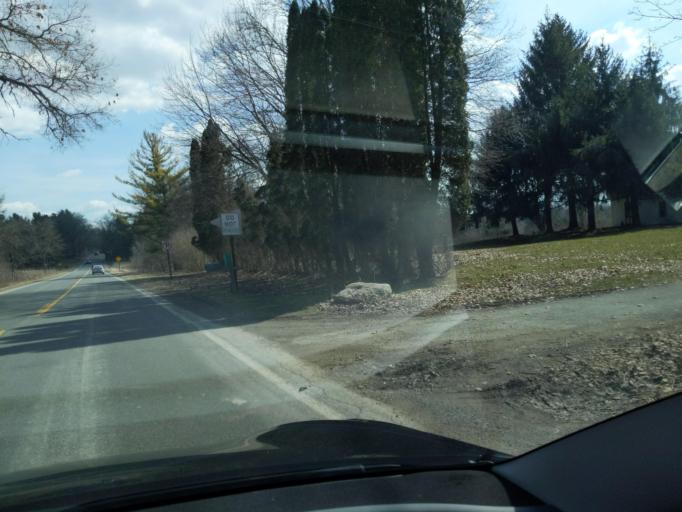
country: US
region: Michigan
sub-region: Livingston County
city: Pinckney
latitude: 42.3923
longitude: -83.9392
